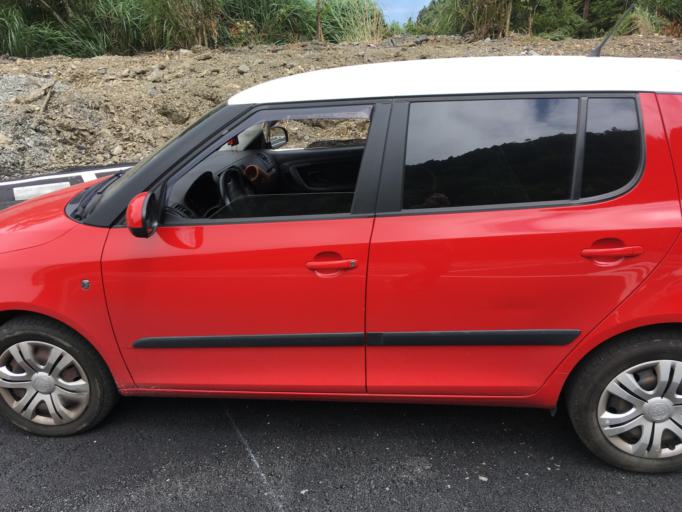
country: TW
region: Taiwan
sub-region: Yilan
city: Yilan
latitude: 24.4996
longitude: 121.5326
